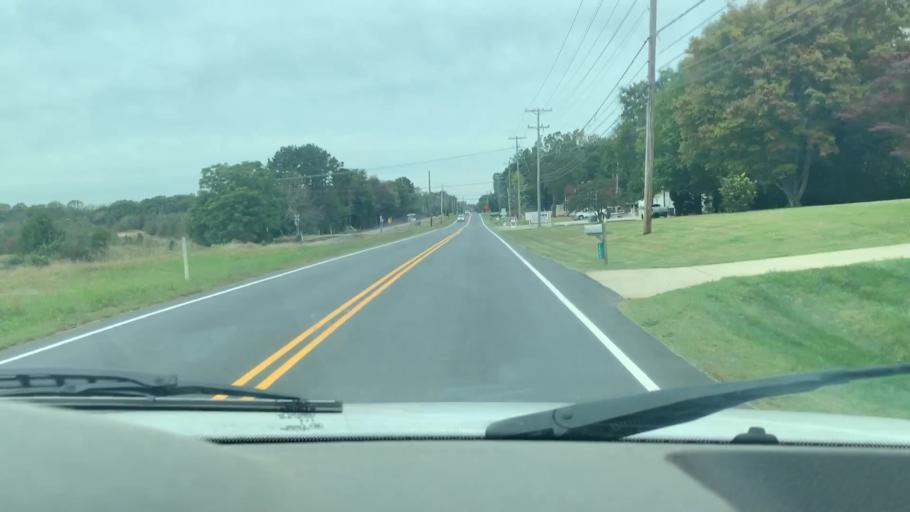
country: US
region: North Carolina
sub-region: Gaston County
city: Davidson
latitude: 35.5203
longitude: -80.8412
